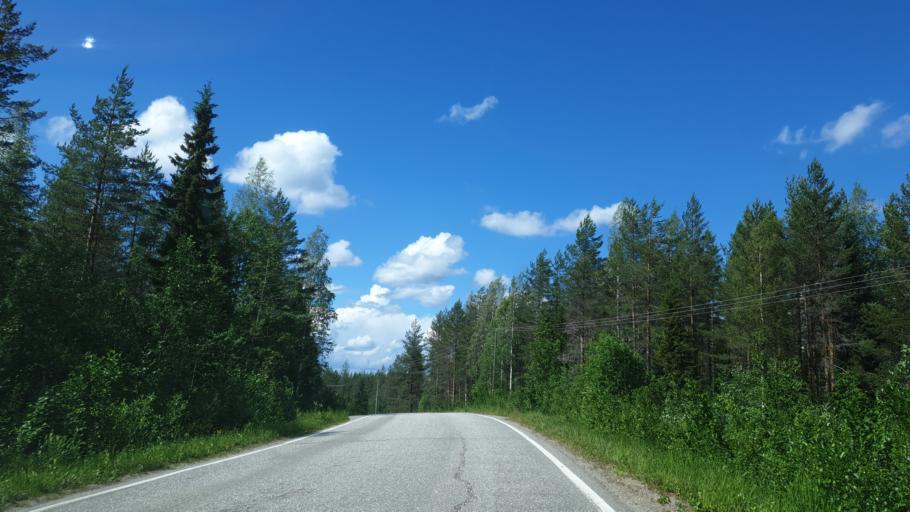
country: FI
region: Northern Savo
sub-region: Koillis-Savo
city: Kaavi
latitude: 63.0402
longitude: 28.5971
